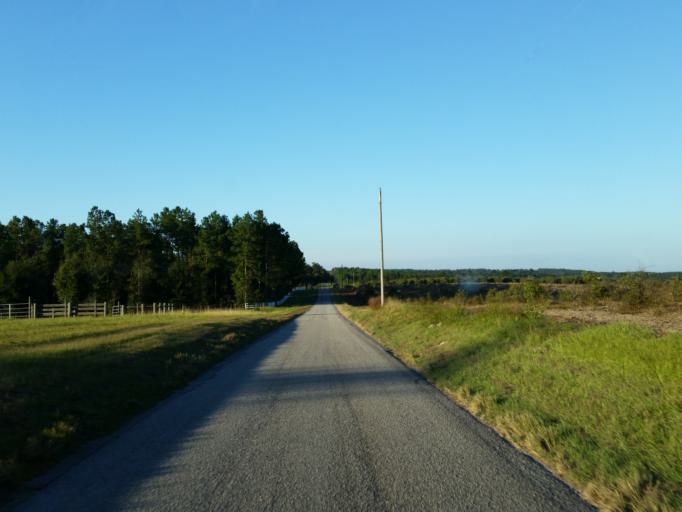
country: US
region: Florida
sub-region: Pasco County
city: Dade City North
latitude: 28.4313
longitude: -82.2698
